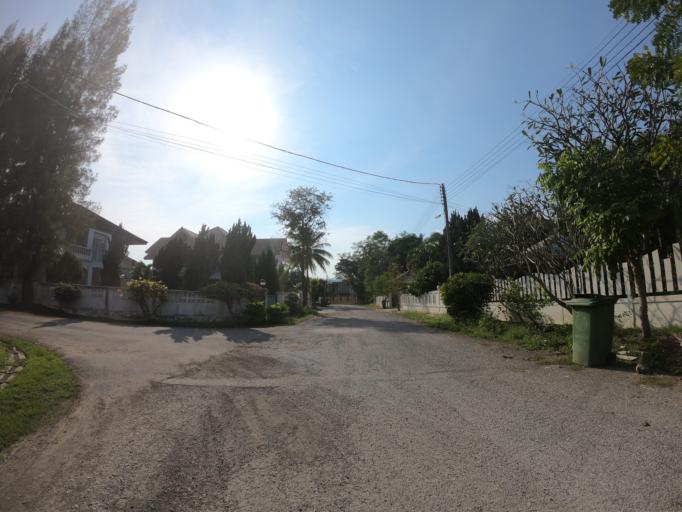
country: TH
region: Chiang Mai
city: San Sai
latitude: 18.8365
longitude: 99.0056
